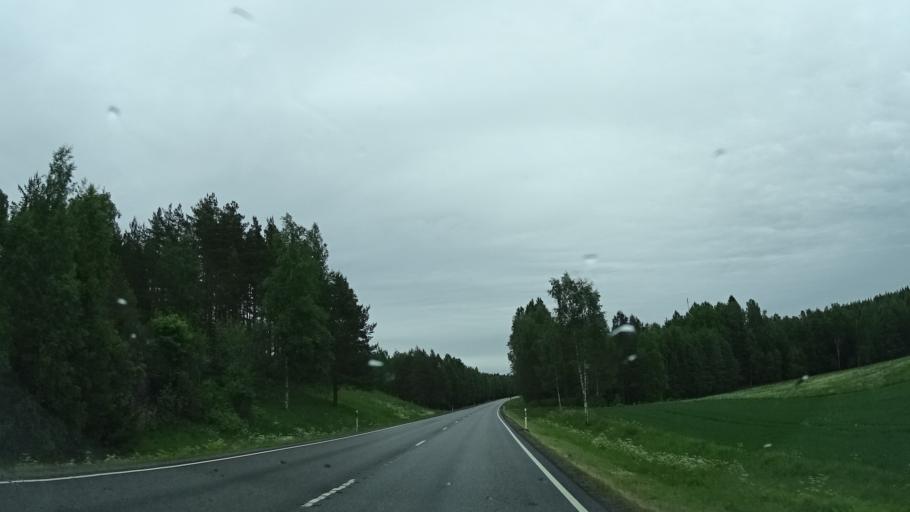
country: FI
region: Varsinais-Suomi
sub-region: Salo
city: Pernioe
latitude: 60.0797
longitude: 23.2494
